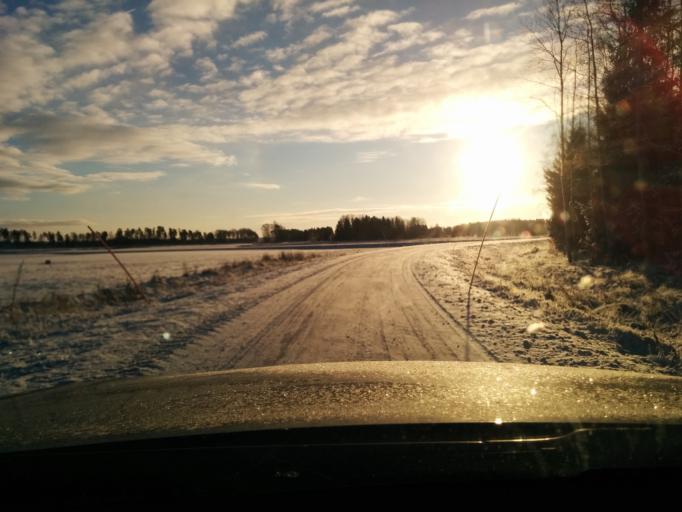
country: SE
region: Uppsala
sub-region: Tierps Kommun
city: Orbyhus
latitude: 60.1821
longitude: 17.6112
